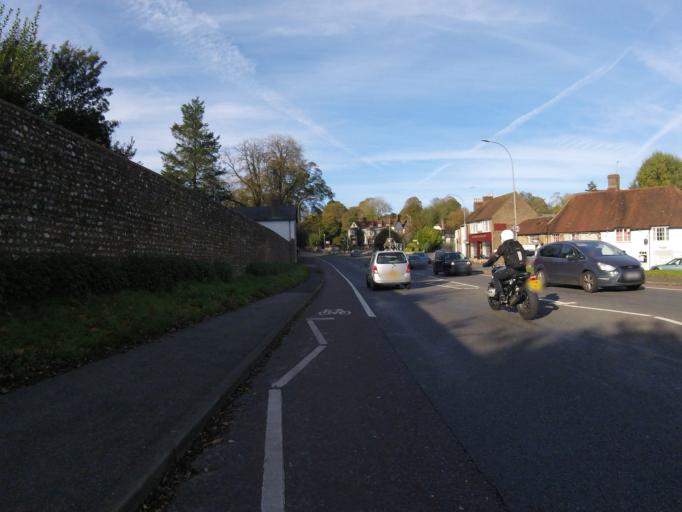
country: GB
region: England
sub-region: Brighton and Hove
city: Hove
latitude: 50.8643
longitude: -0.1522
